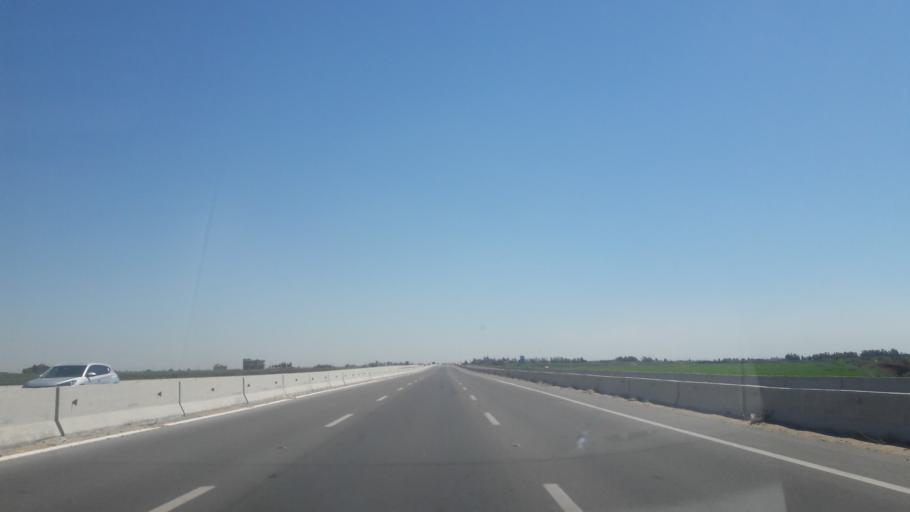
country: EG
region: Al Isma'iliyah
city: Ismailia
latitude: 30.8943
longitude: 32.1776
